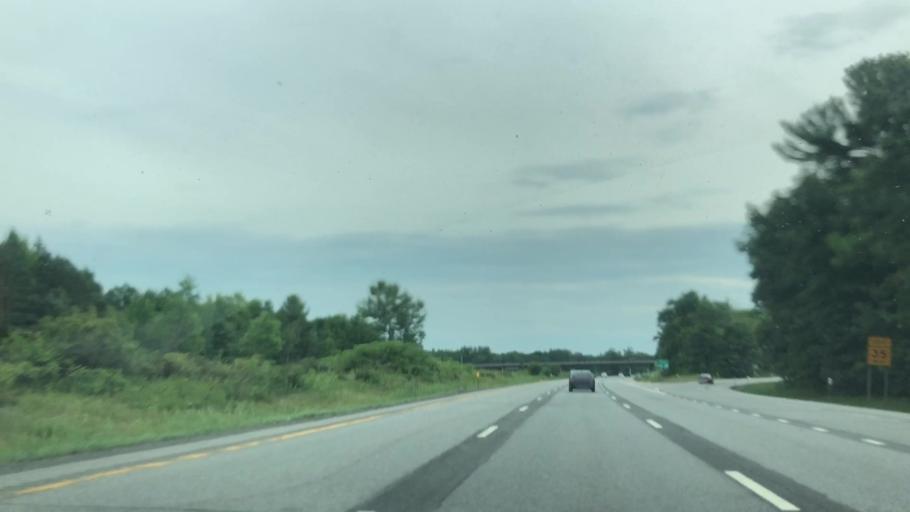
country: US
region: New York
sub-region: Saratoga County
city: Saratoga Springs
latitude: 43.0749
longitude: -73.7501
